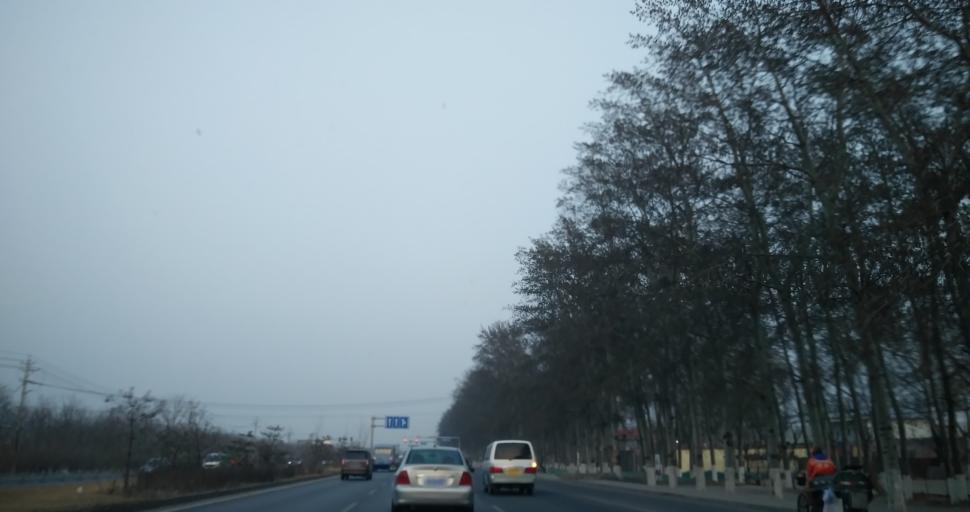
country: CN
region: Beijing
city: Xingfeng
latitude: 39.7205
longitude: 116.3574
